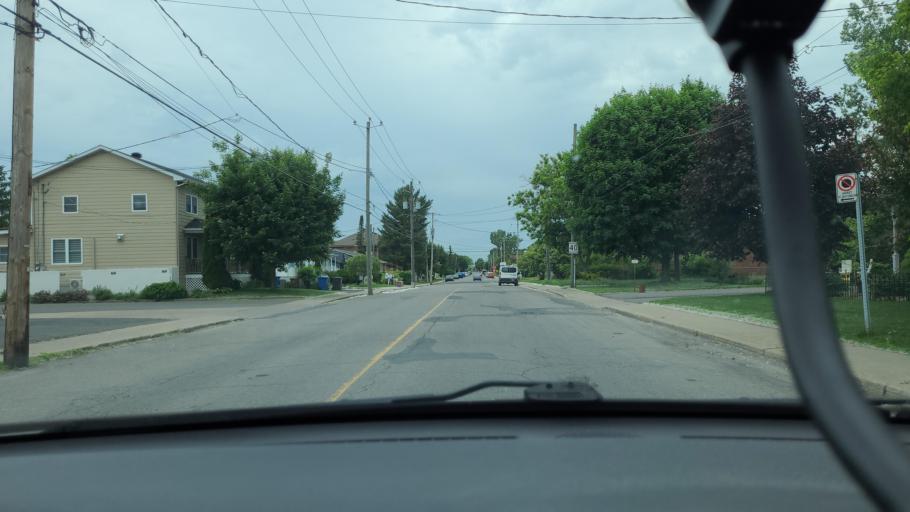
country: CA
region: Quebec
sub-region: Monteregie
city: La Prairie
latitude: 45.4143
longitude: -73.4914
